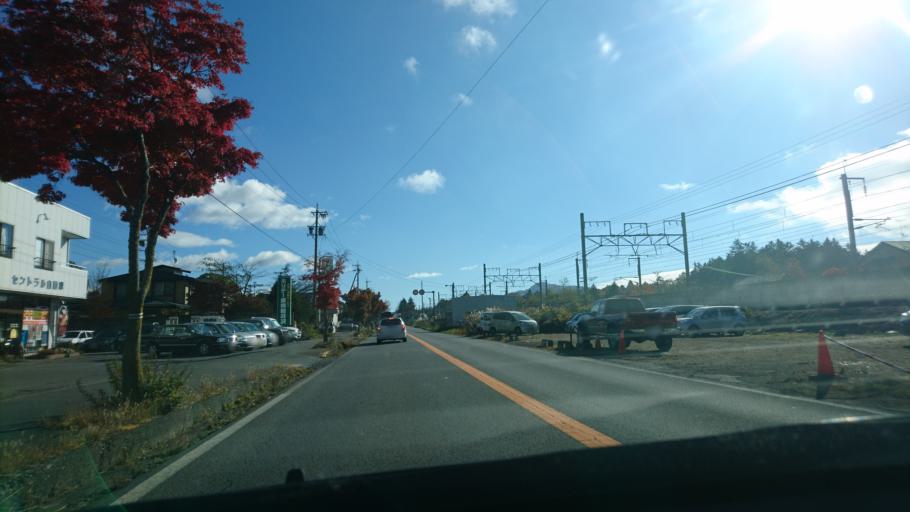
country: JP
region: Nagano
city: Komoro
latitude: 36.3438
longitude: 138.6098
